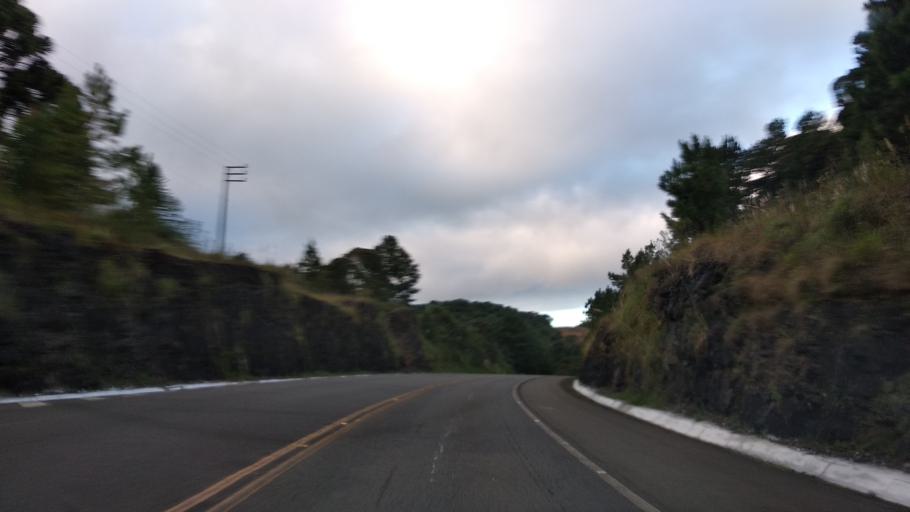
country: BR
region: Santa Catarina
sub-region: Campos Novos
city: Campos Novos
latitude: -27.5013
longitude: -50.9288
